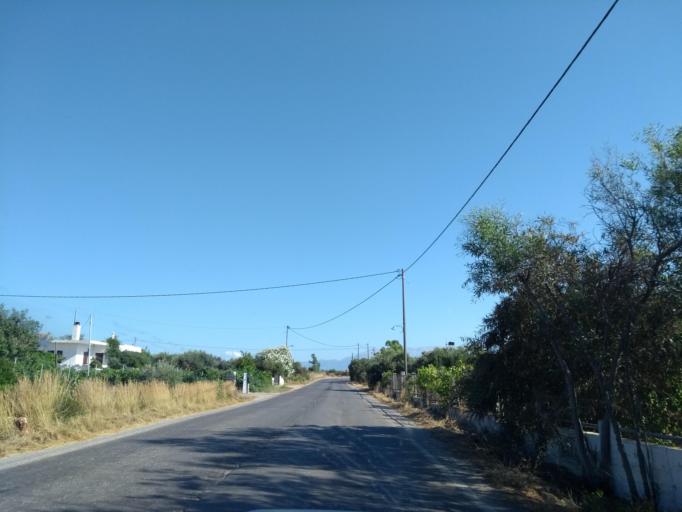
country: GR
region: Crete
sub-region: Nomos Chanias
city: Pithari
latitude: 35.5794
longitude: 24.0937
